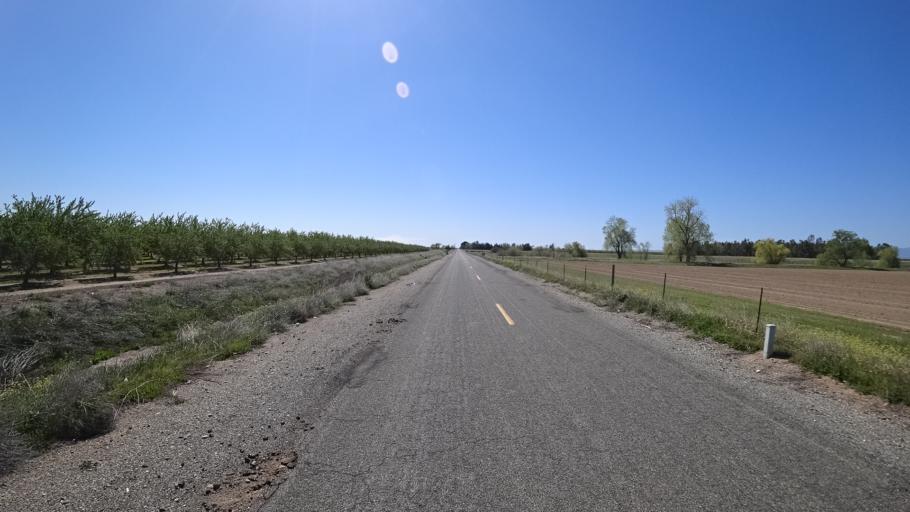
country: US
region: California
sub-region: Glenn County
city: Orland
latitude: 39.6874
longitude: -122.2530
